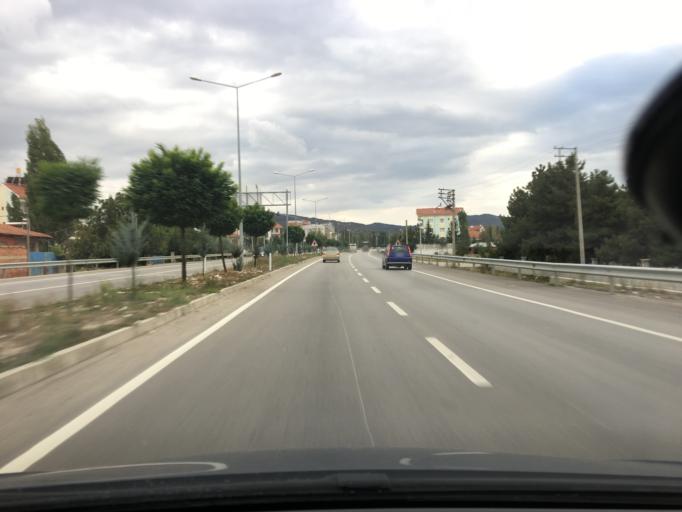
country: TR
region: Afyonkarahisar
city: Sincanli
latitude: 38.7305
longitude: 30.3458
